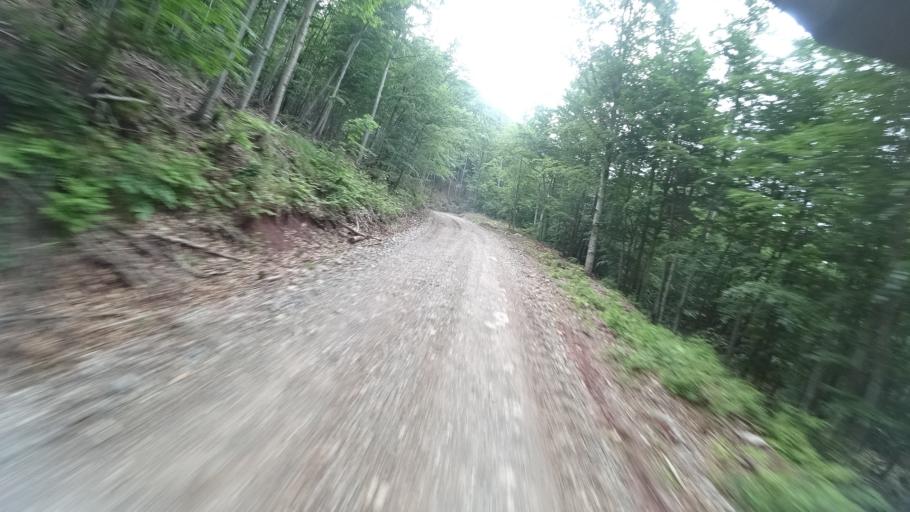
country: HR
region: Zadarska
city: Obrovac
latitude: 44.2884
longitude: 15.6778
